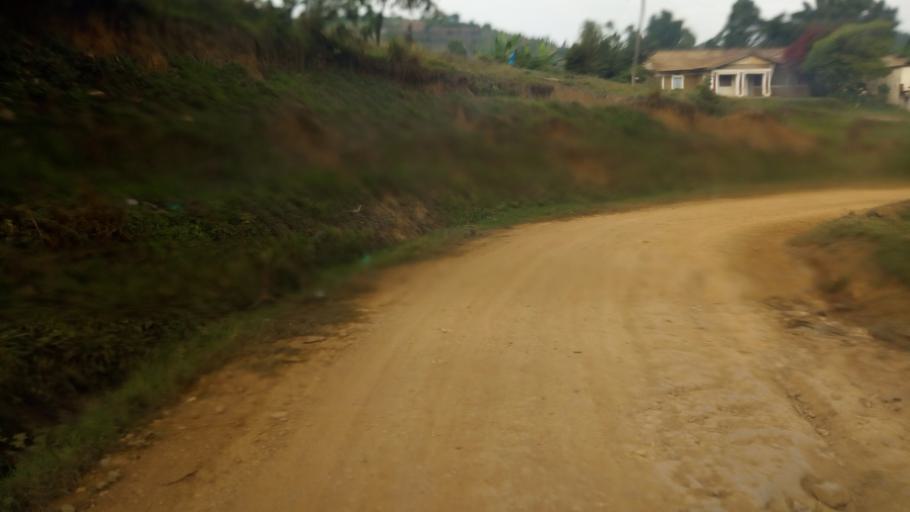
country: UG
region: Western Region
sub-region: Kanungu District
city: Ntungamo
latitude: -0.8293
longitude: 29.7097
